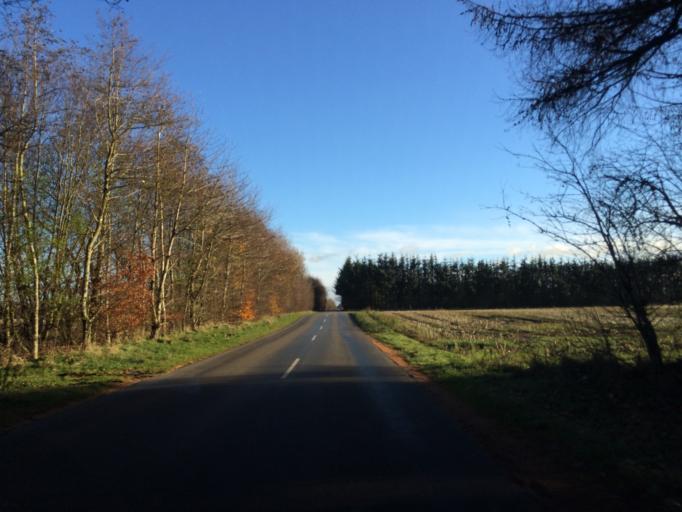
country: DK
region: Central Jutland
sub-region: Herning Kommune
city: Kibaek
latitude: 56.0539
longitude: 8.7868
